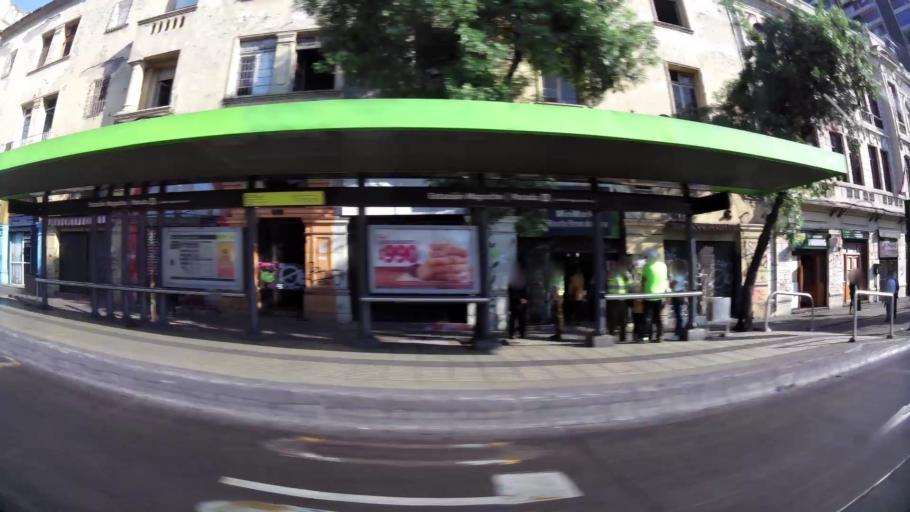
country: CL
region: Santiago Metropolitan
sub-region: Provincia de Santiago
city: Santiago
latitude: -33.4332
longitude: -70.6526
